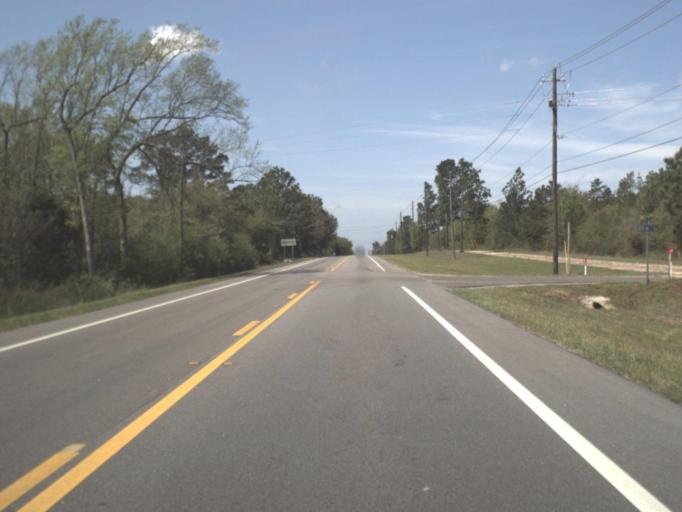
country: US
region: Florida
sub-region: Santa Rosa County
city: East Milton
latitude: 30.6389
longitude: -86.9546
